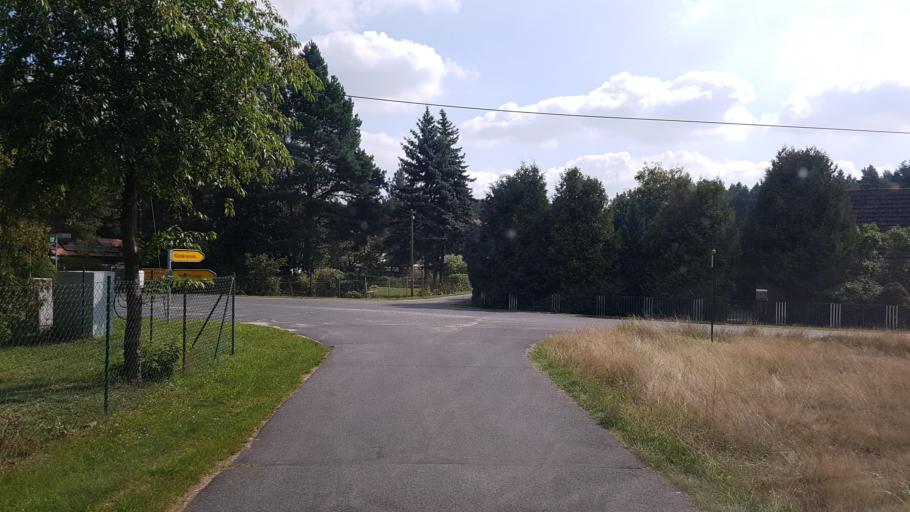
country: DE
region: Brandenburg
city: Schonewalde
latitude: 51.7505
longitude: 13.5536
